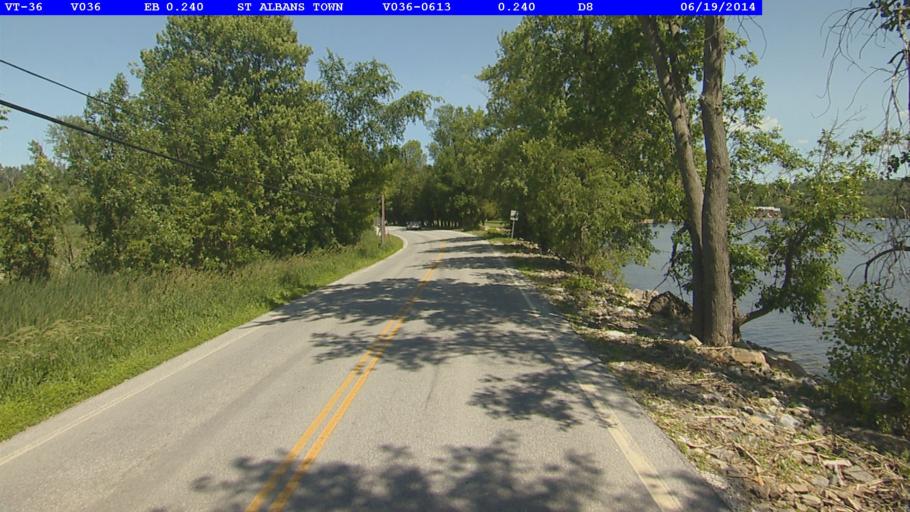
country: US
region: Vermont
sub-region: Franklin County
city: Saint Albans
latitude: 44.8102
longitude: -73.1467
